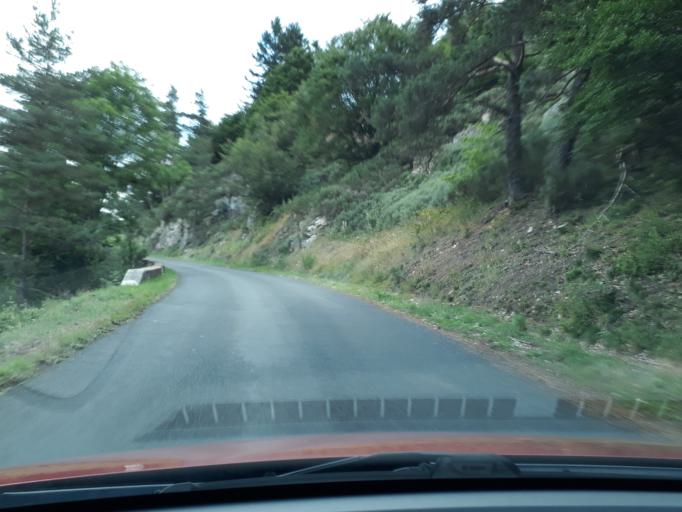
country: FR
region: Auvergne
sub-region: Departement de la Haute-Loire
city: Le Monastier-sur-Gazeille
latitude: 44.8272
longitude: 3.9452
